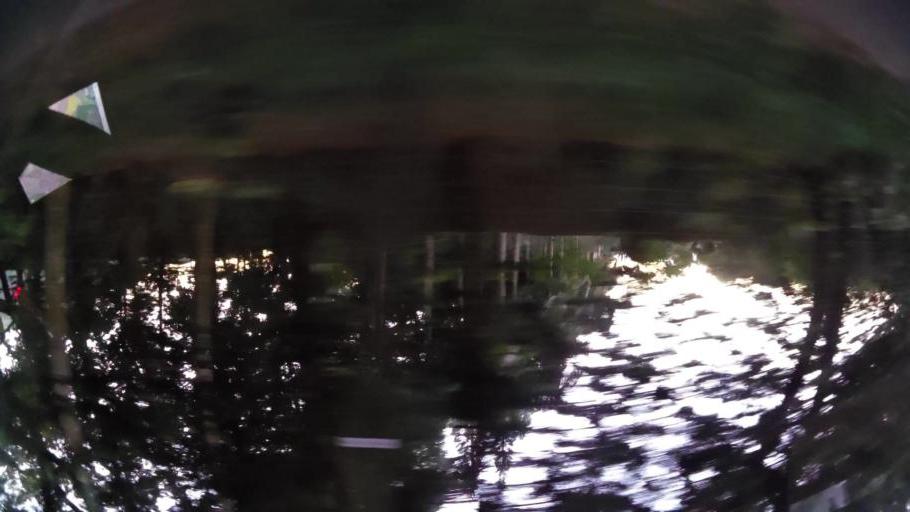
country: MU
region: Moka
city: Moka
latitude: -20.2232
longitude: 57.5011
